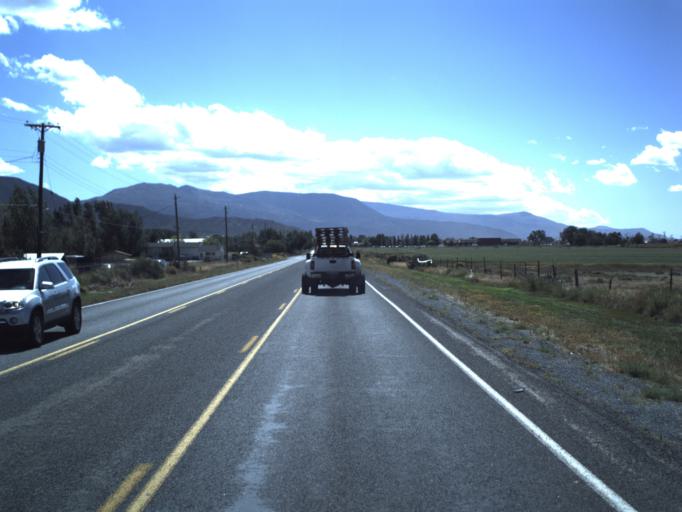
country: US
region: Utah
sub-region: Iron County
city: Enoch
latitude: 37.7575
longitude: -113.0553
